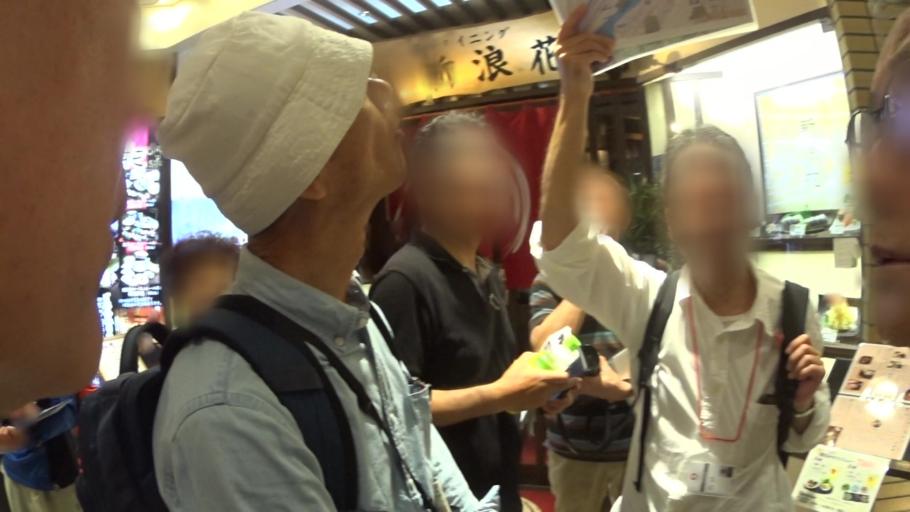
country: JP
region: Osaka
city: Osaka-shi
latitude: 34.7010
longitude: 135.4940
